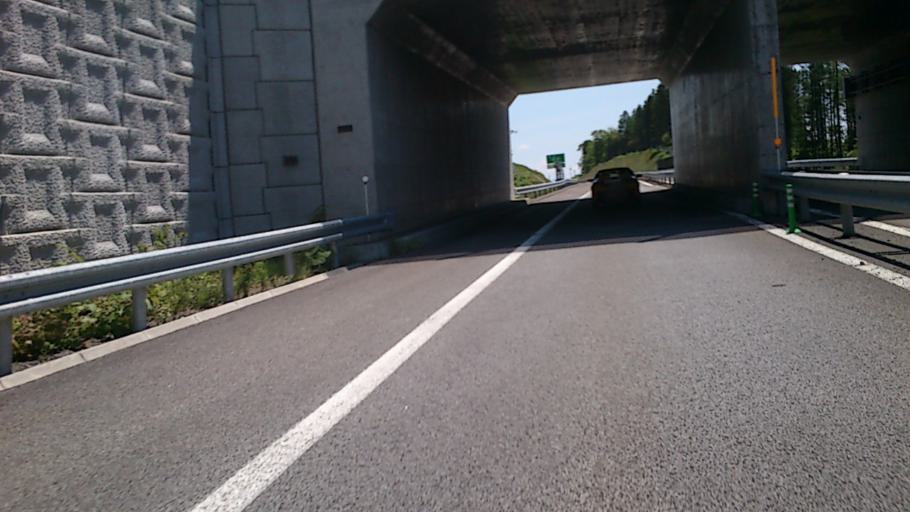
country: JP
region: Hokkaido
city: Nayoro
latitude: 44.4868
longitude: 142.3621
